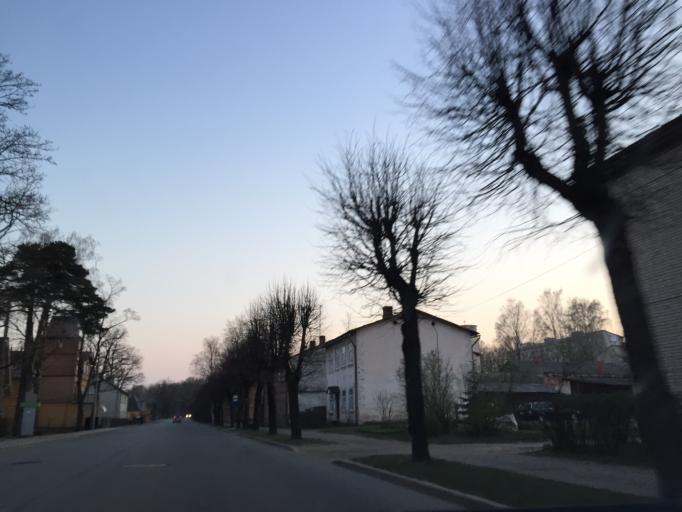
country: LV
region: Valkas Rajons
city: Valka
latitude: 57.7721
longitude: 26.0166
